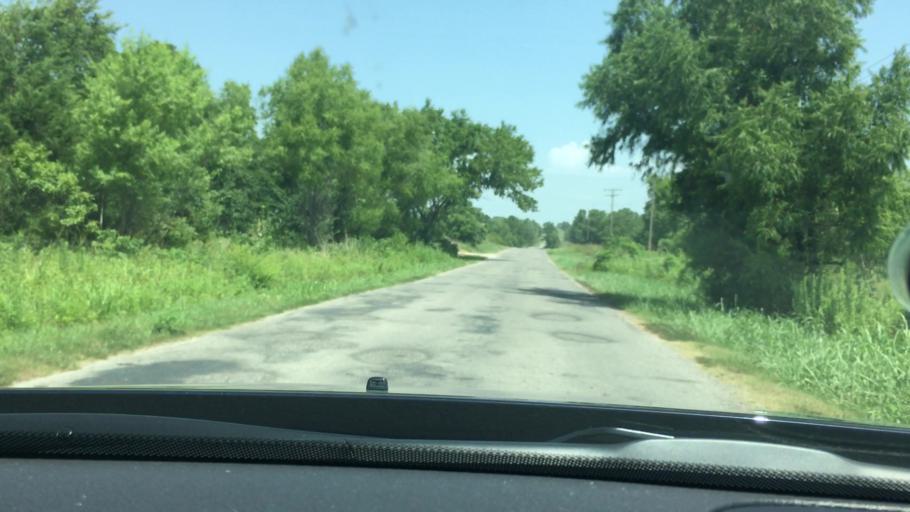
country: US
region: Oklahoma
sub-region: Pontotoc County
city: Byng
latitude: 34.8354
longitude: -96.6697
